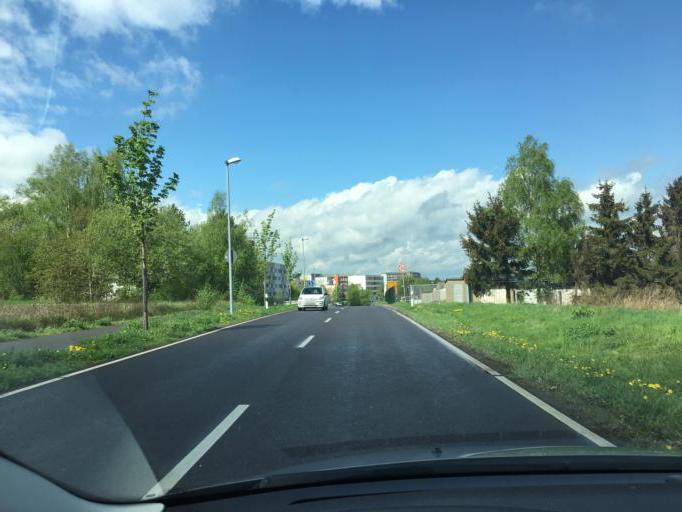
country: DE
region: Saxony-Anhalt
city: Haldensleben I
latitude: 52.2787
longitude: 11.3985
